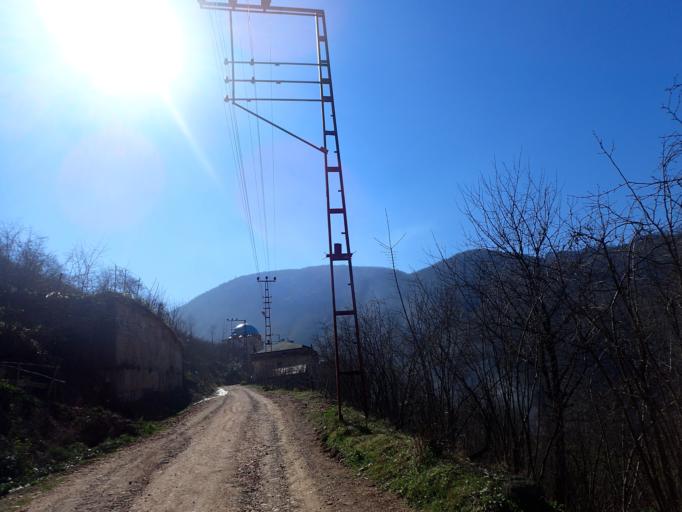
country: TR
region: Ordu
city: Catalpinar
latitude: 40.8672
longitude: 37.4949
